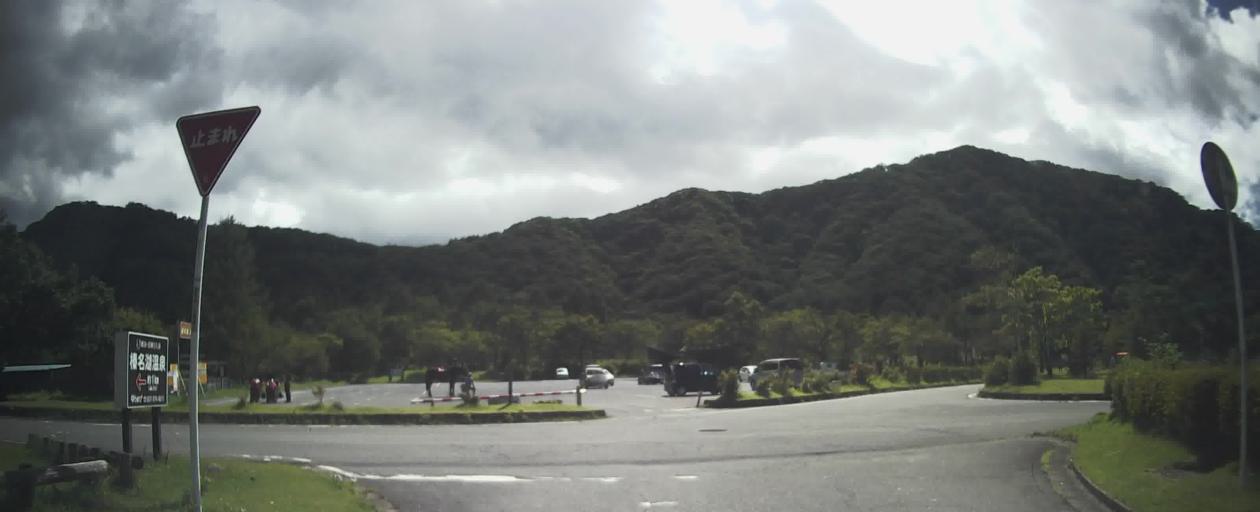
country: JP
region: Gunma
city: Nakanojomachi
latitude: 36.4712
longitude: 138.8742
